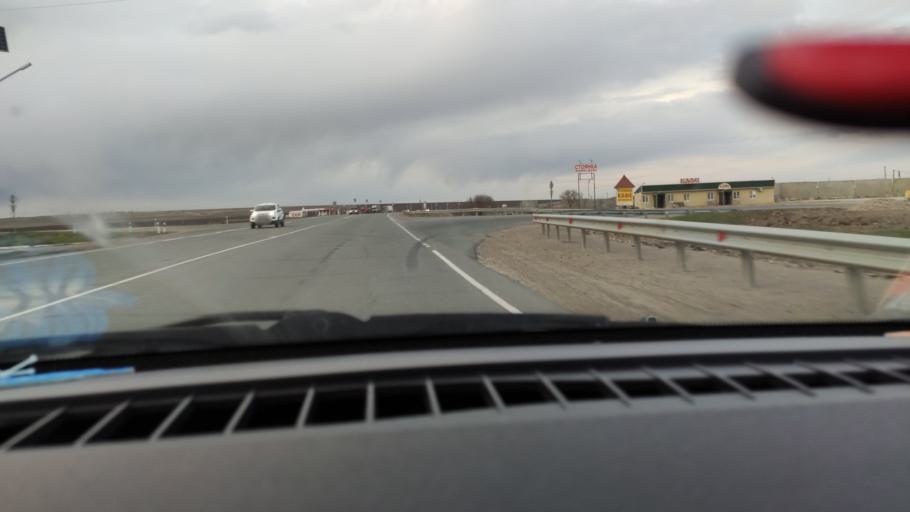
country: RU
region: Saratov
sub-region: Saratovskiy Rayon
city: Saratov
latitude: 51.7354
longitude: 46.0368
